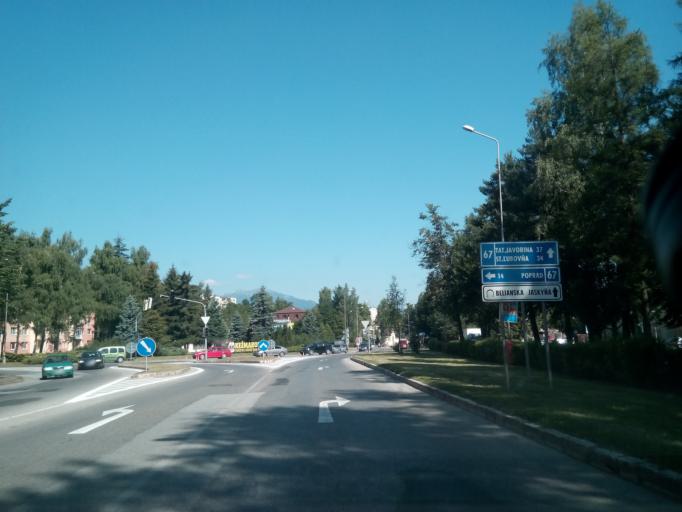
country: SK
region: Presovsky
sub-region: Okres Presov
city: Kezmarok
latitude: 49.1339
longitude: 20.4289
